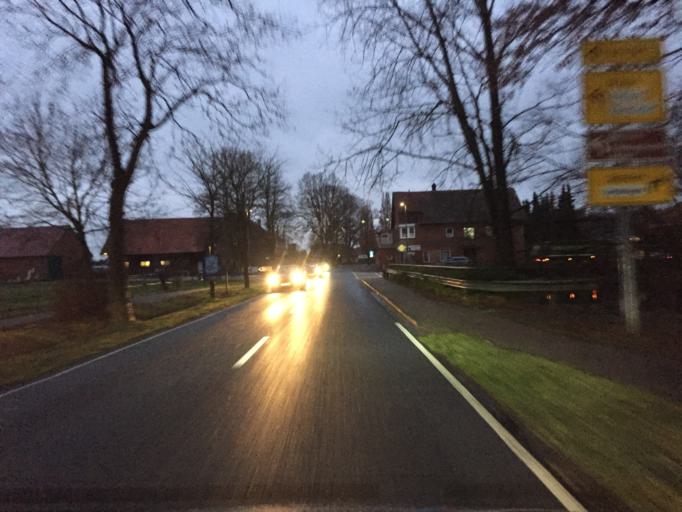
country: DE
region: Lower Saxony
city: Schwaforden
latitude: 52.7384
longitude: 8.8188
